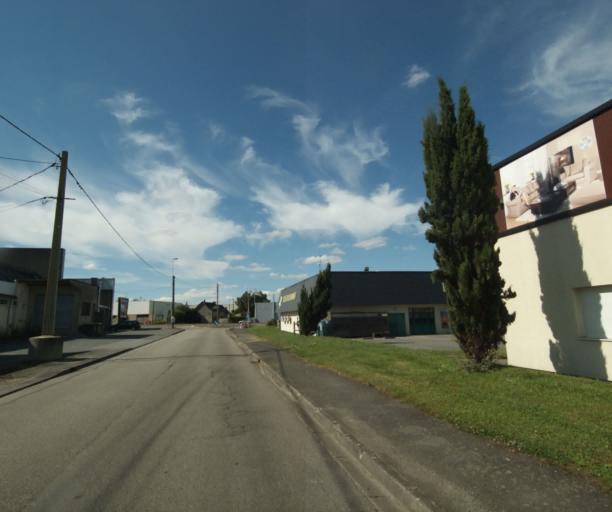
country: FR
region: Pays de la Loire
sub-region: Departement de la Mayenne
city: Laval
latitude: 48.0686
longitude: -0.7949
